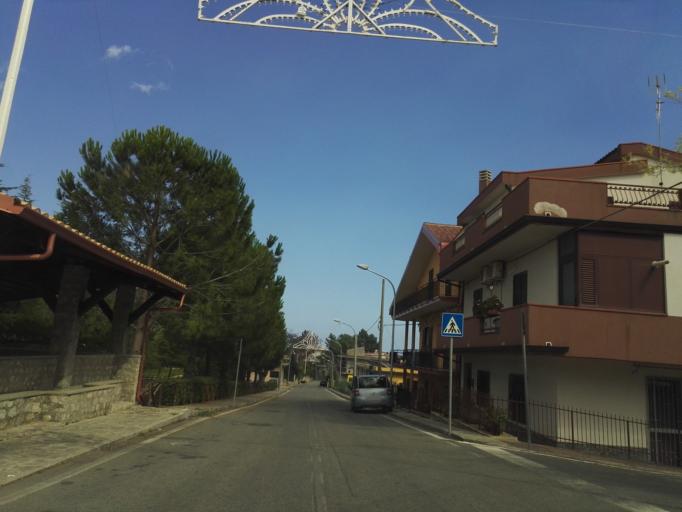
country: IT
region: Calabria
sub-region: Provincia di Reggio Calabria
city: Camini
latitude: 38.4309
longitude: 16.4839
